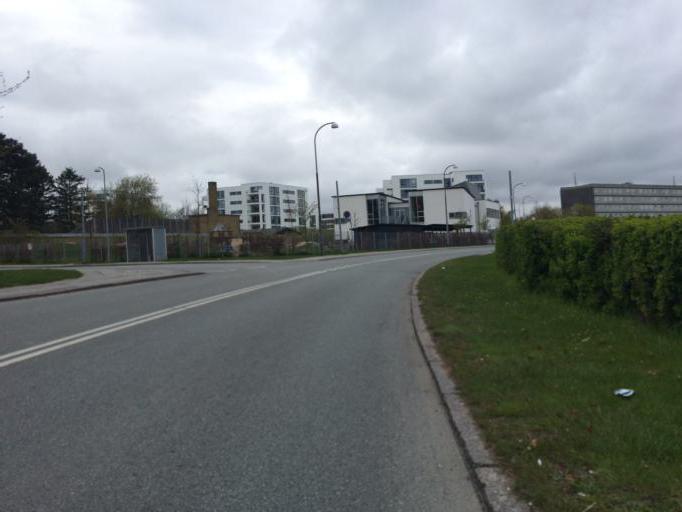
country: DK
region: Capital Region
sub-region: Vallensbaek Kommune
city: Vallensbaek
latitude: 55.6236
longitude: 12.3803
